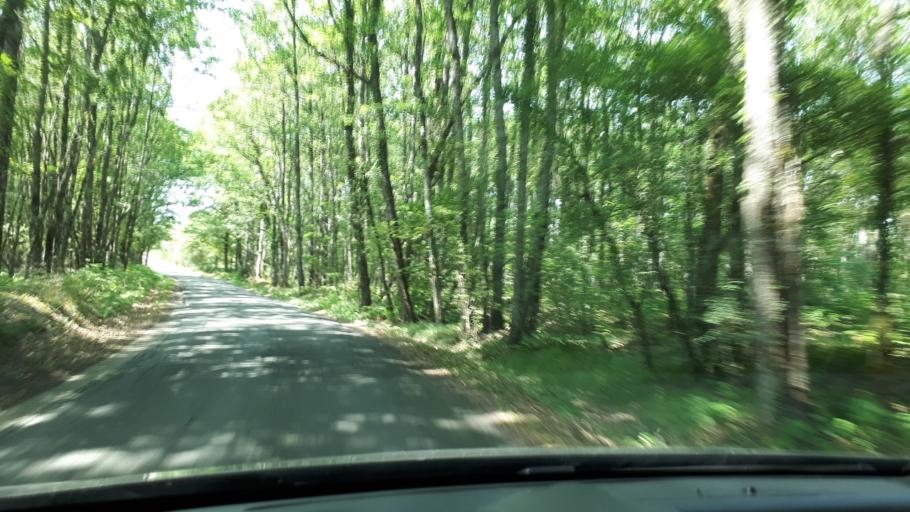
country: FR
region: Centre
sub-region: Departement du Loir-et-Cher
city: Aze
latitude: 47.8359
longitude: 1.0310
